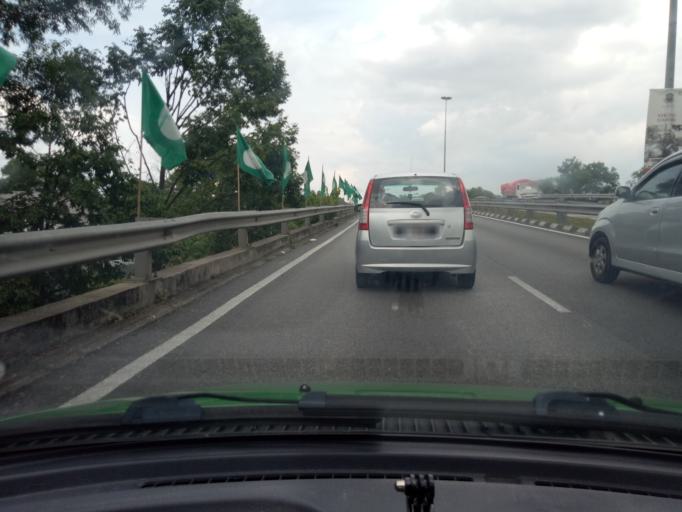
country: MY
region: Selangor
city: Kampong Baharu Balakong
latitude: 3.0105
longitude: 101.7993
